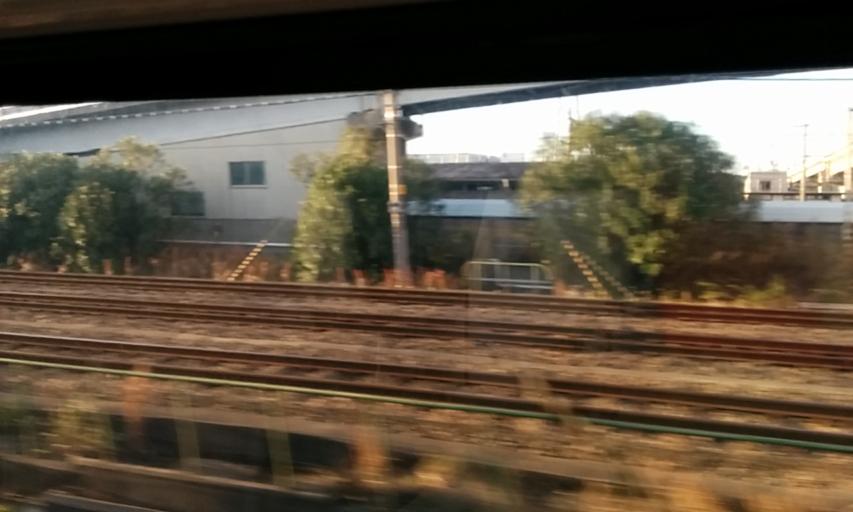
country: JP
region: Aichi
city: Kasugai
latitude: 35.2544
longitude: 137.0062
